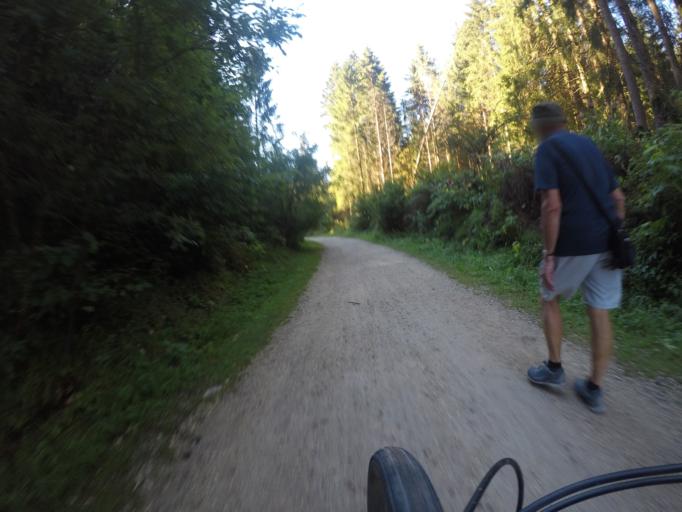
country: IT
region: Veneto
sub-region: Provincia di Vicenza
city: Canove di Roana
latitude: 45.8523
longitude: 11.4769
